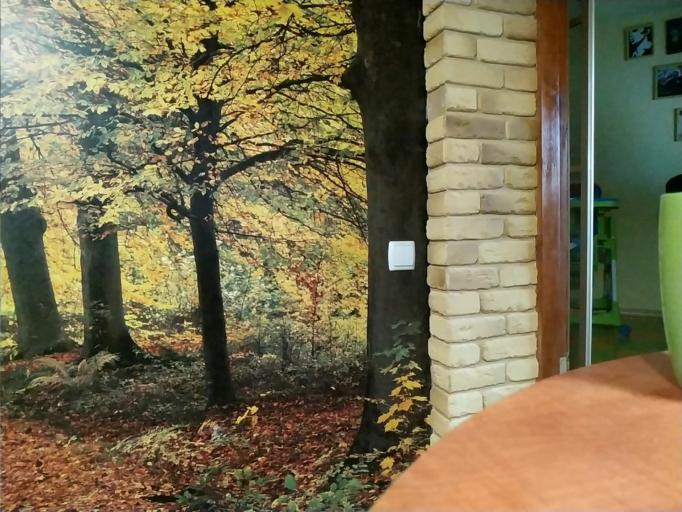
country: RU
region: Tverskaya
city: Staraya Toropa
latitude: 56.3494
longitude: 31.8196
